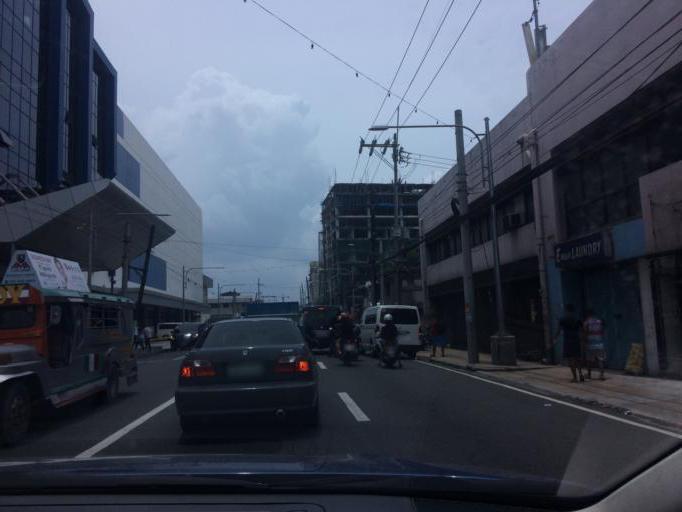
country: PH
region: Metro Manila
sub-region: Makati City
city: Makati City
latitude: 14.5217
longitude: 120.9968
